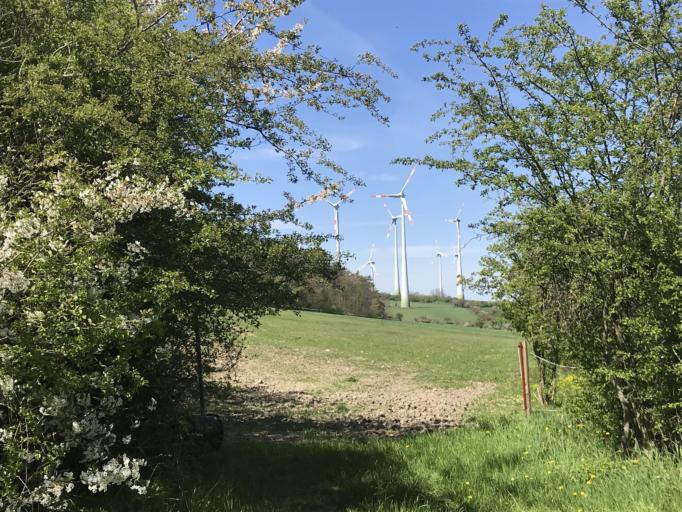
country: DE
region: Saxony-Anhalt
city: Huy-Neinstedt
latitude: 51.9762
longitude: 10.8782
